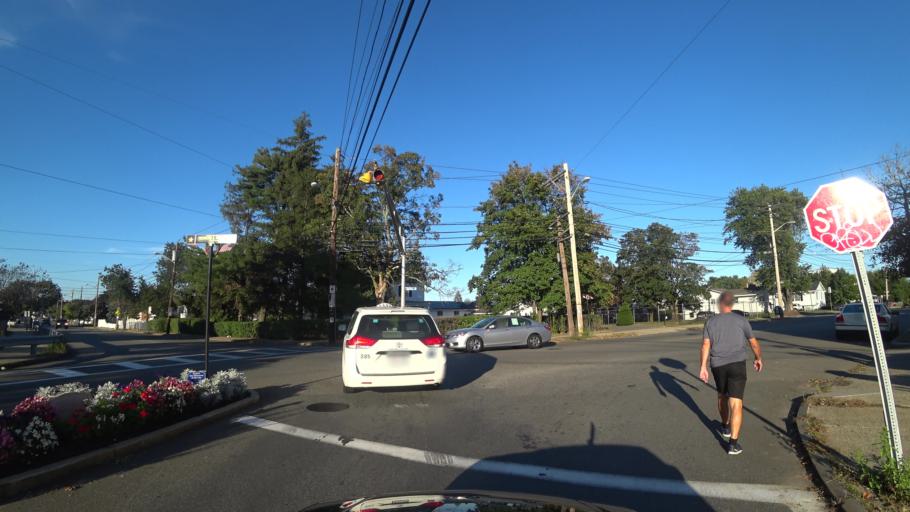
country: US
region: Massachusetts
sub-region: Suffolk County
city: Revere
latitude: 42.4210
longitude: -71.0173
